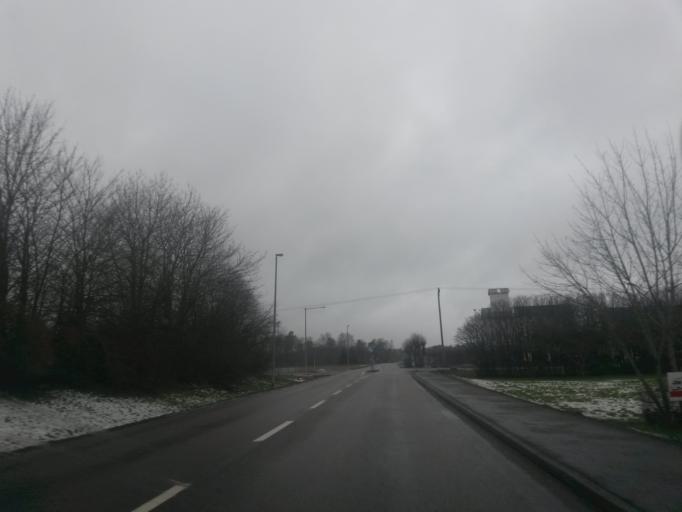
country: SE
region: Vaestra Goetaland
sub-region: Alingsas Kommun
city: Sollebrunn
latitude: 58.1227
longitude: 12.5205
